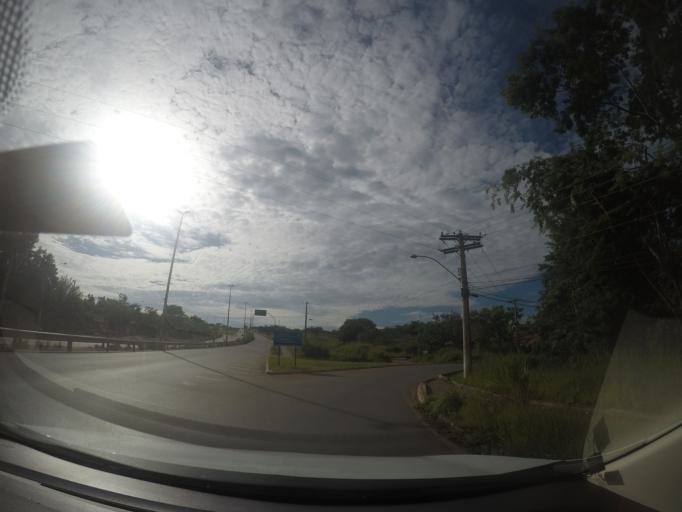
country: BR
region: Goias
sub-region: Goiania
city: Goiania
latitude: -16.6860
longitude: -49.1884
